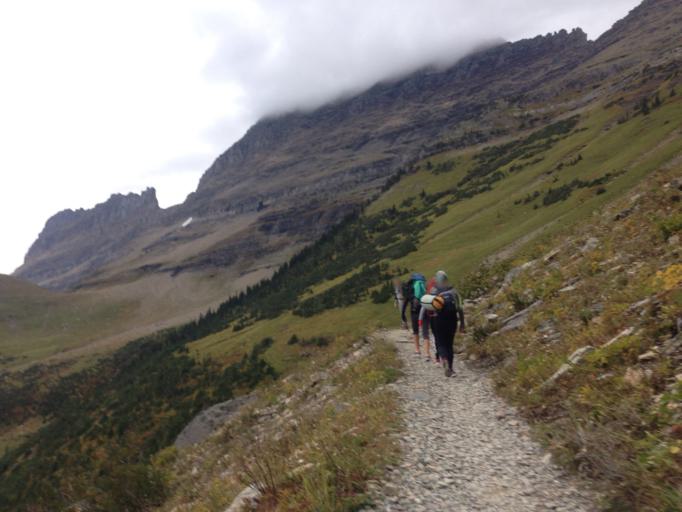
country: US
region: Montana
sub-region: Flathead County
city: Columbia Falls
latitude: 48.7262
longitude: -113.7186
